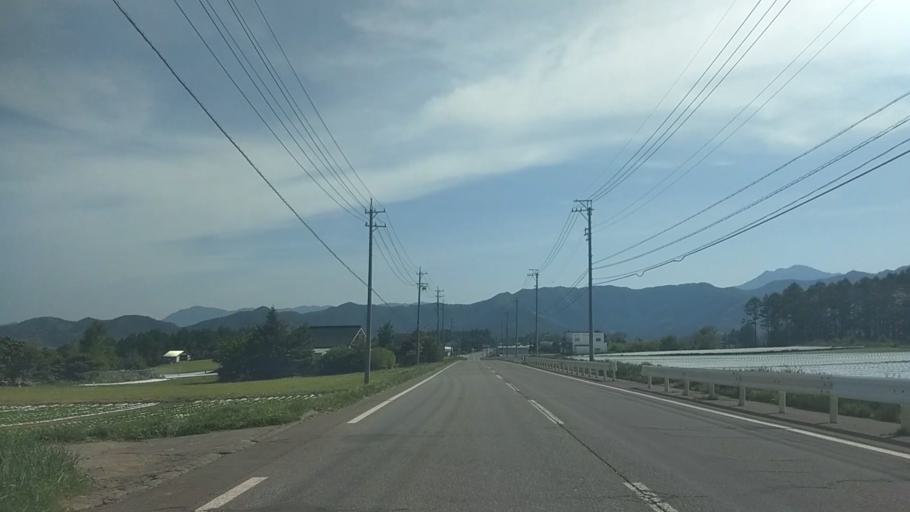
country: JP
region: Nagano
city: Saku
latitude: 35.9925
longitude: 138.4921
